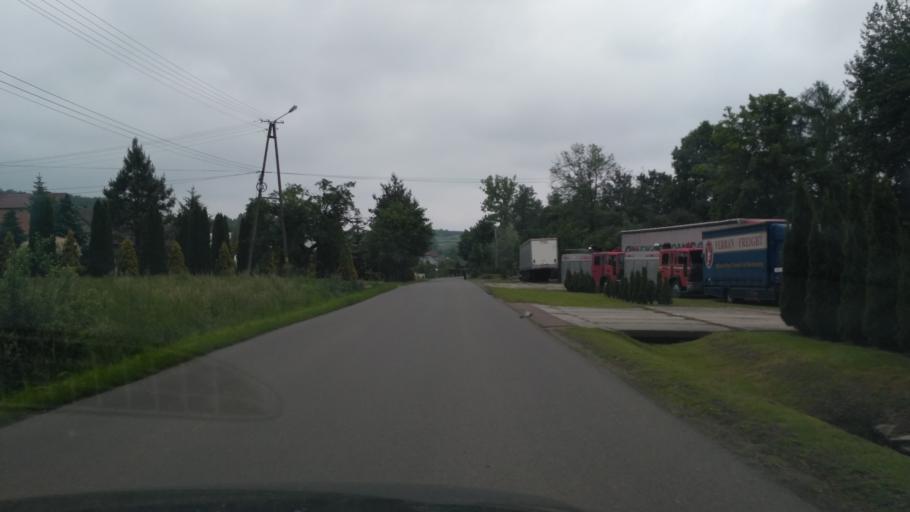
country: PL
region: Subcarpathian Voivodeship
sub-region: Powiat ropczycko-sedziszowski
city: Zagorzyce
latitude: 50.0210
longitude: 21.6787
